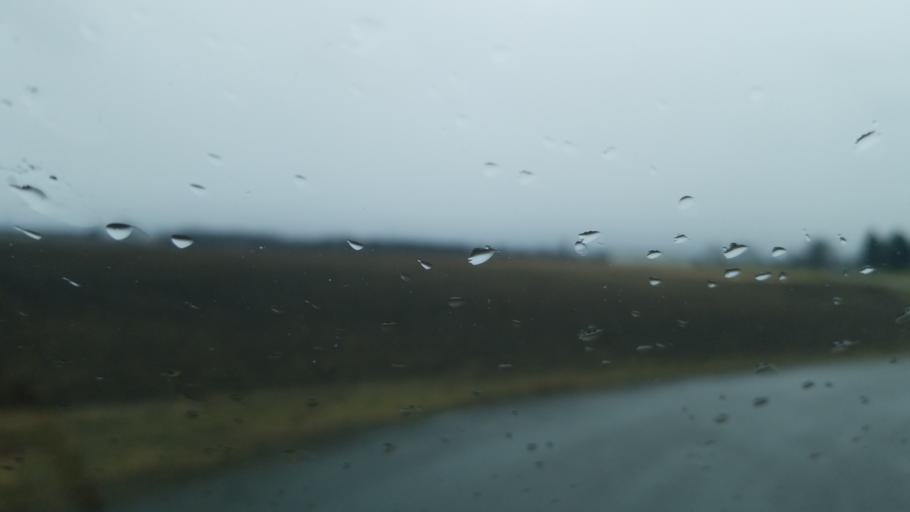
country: US
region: Ohio
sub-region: Hardin County
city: Kenton
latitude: 40.5505
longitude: -83.6537
